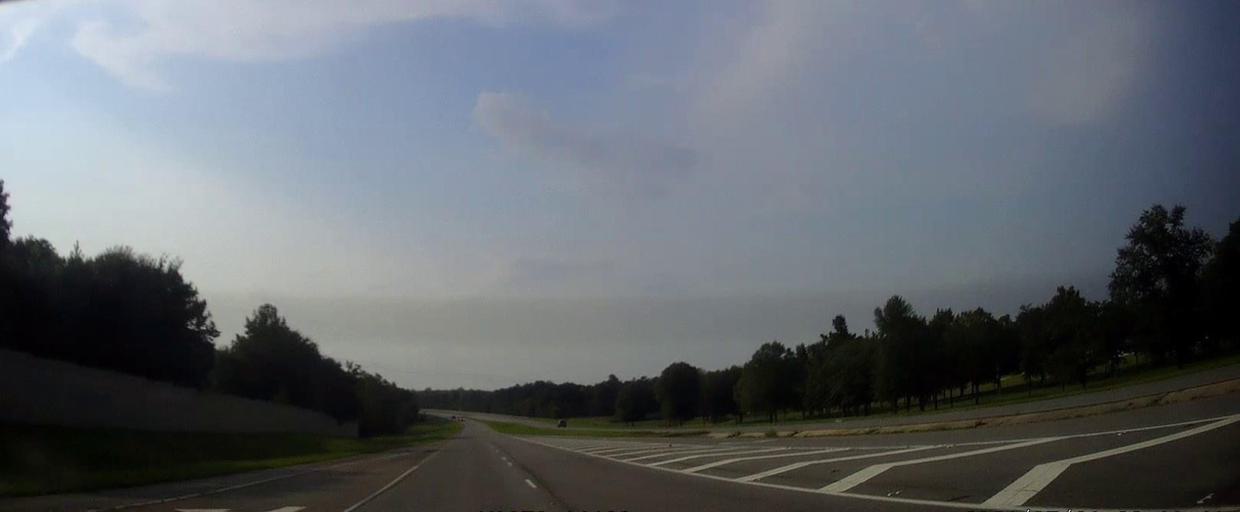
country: US
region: Georgia
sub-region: Laurens County
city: Dublin
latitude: 32.5359
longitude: -82.9705
